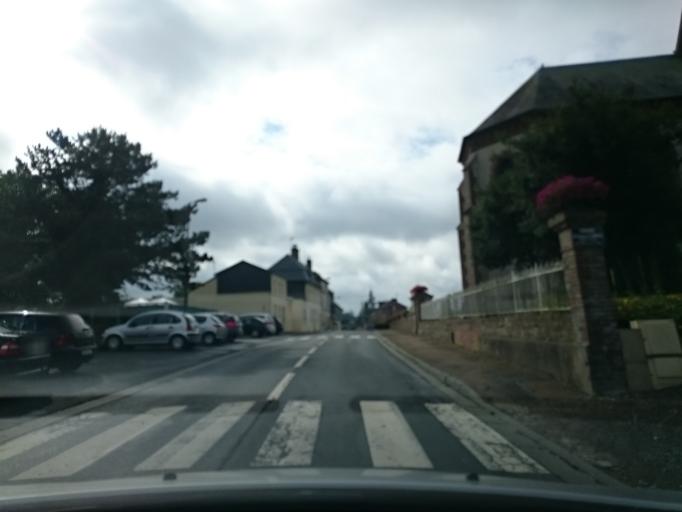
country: FR
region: Lower Normandy
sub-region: Departement du Calvados
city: Beuvillers
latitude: 49.1244
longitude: 0.2773
